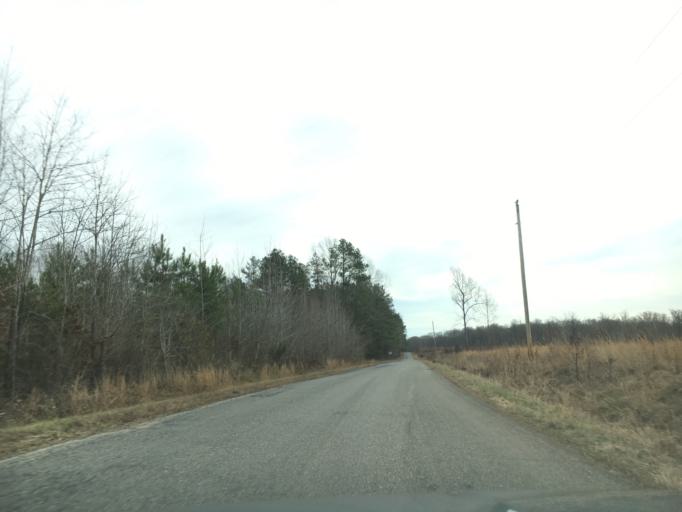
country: US
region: Virginia
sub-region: Amelia County
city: Amelia Court House
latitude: 37.4232
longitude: -77.9934
